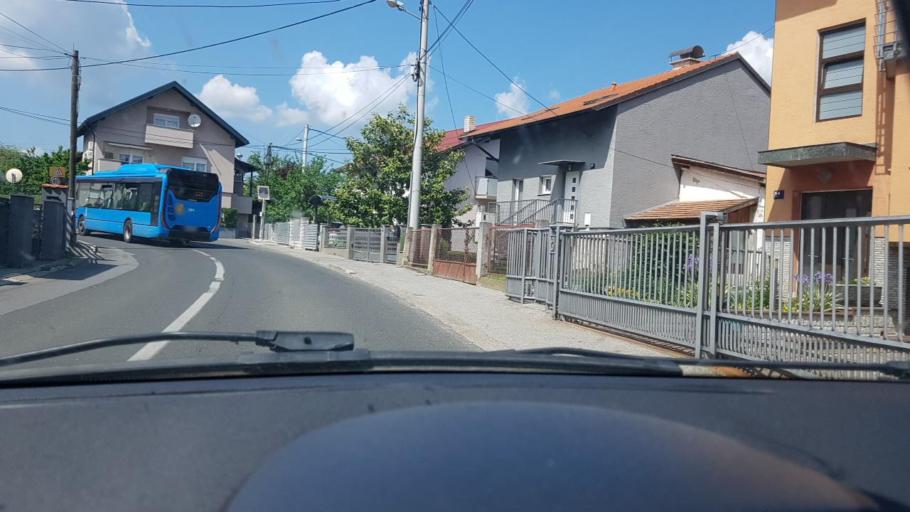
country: HR
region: Grad Zagreb
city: Zagreb
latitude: 45.8394
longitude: 16.0079
